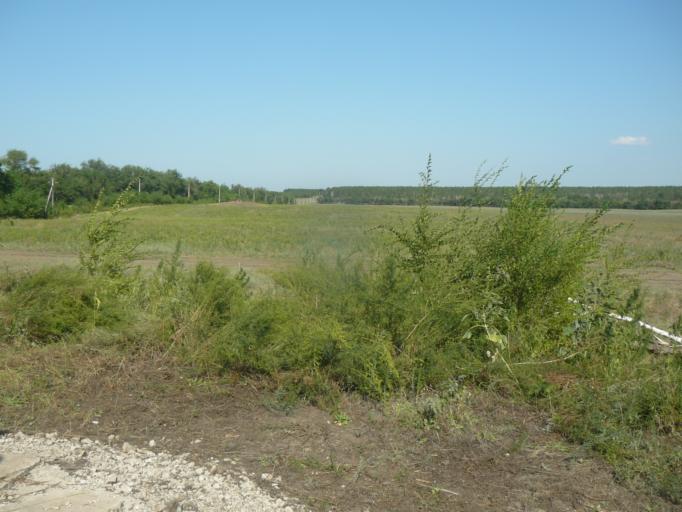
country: RU
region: Saratov
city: Krasnyy Yar
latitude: 51.5937
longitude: 46.5301
